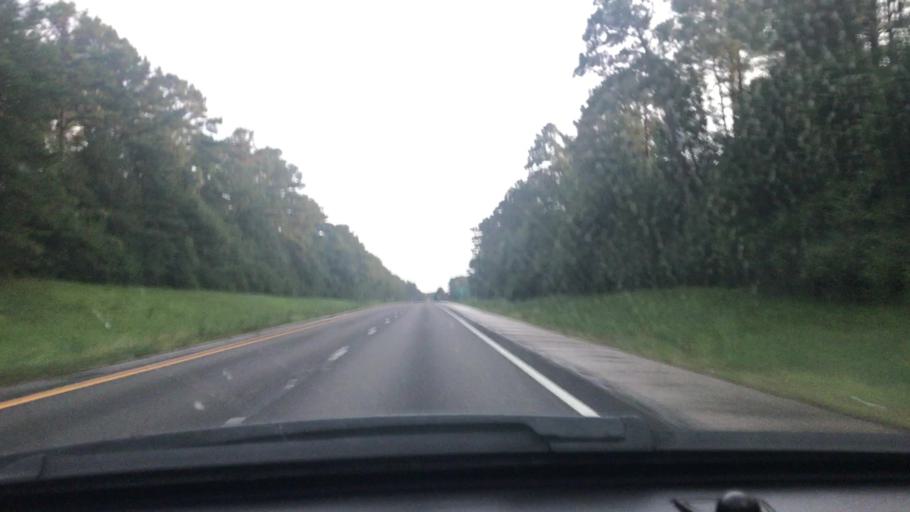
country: US
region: Mississippi
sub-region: Pike County
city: Magnolia
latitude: 31.0706
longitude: -90.4923
